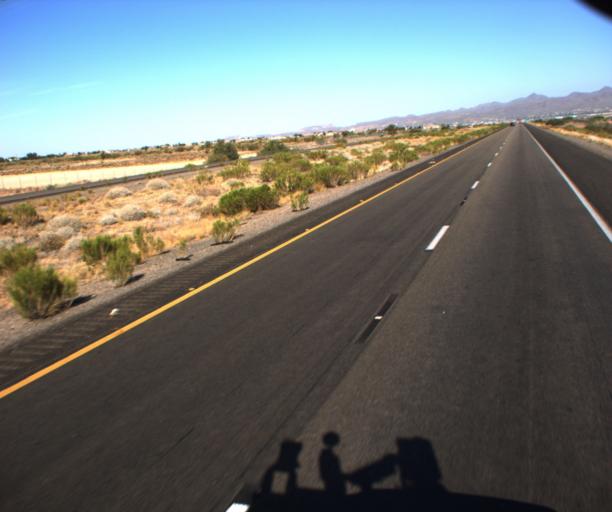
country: US
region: Arizona
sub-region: Mohave County
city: New Kingman-Butler
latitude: 35.2082
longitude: -113.9567
